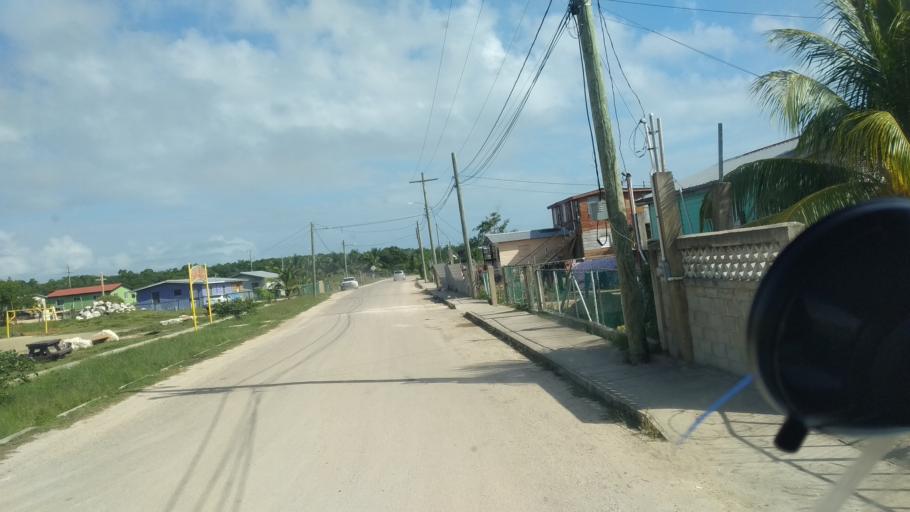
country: BZ
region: Belize
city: Belize City
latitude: 17.5151
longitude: -88.2343
